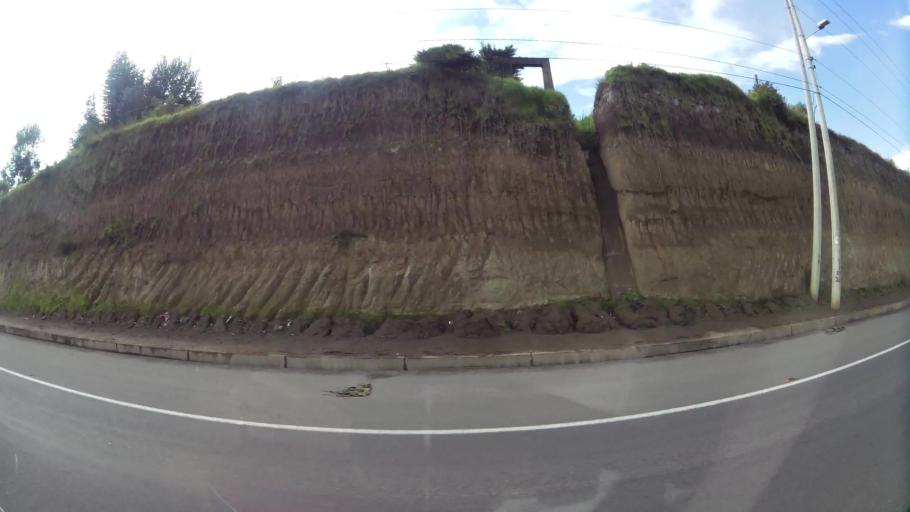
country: EC
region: Pichincha
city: Sangolqui
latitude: -0.3272
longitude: -78.4093
